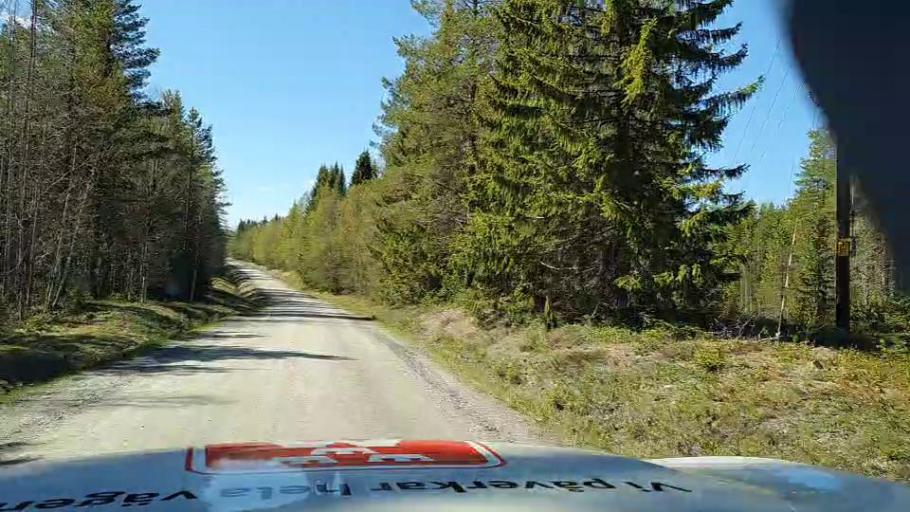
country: SE
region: Jaemtland
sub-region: Krokoms Kommun
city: Valla
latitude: 63.6687
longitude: 13.6938
